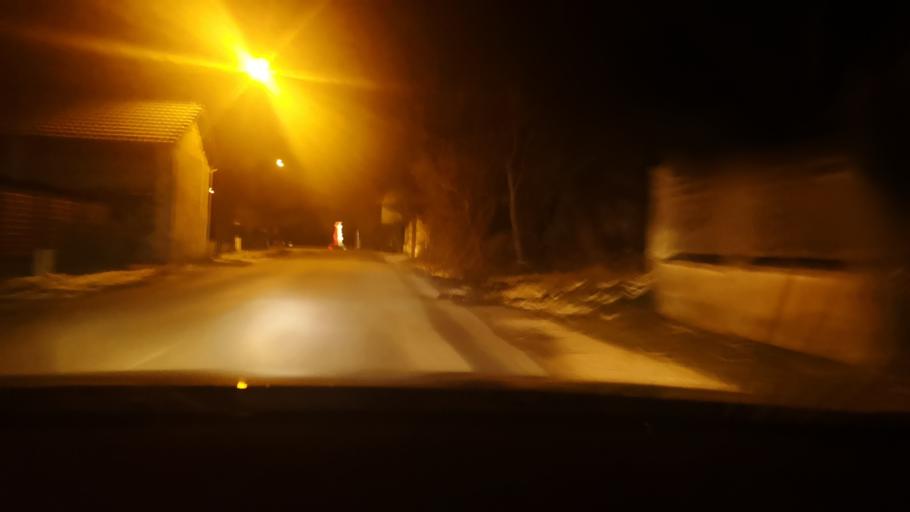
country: FR
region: Bourgogne
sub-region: Departement de Saone-et-Loire
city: Cuisery
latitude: 46.5259
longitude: 5.0109
